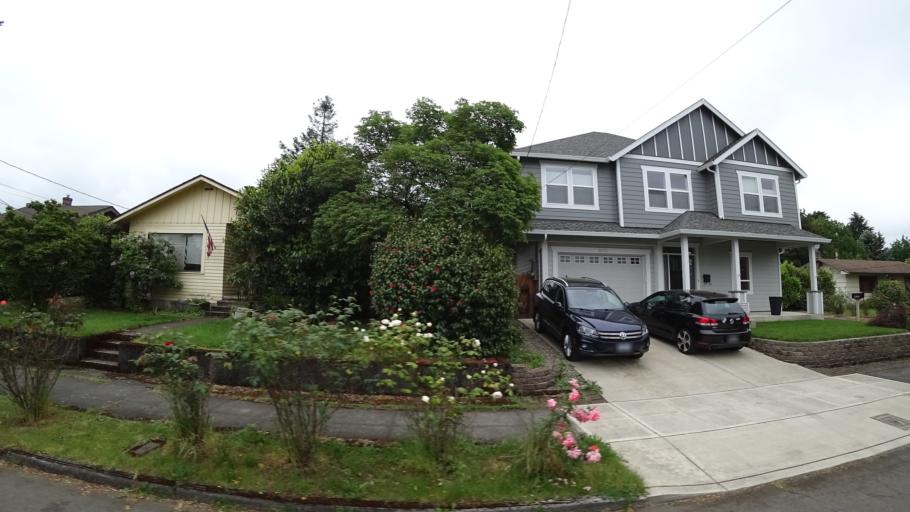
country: US
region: Oregon
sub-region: Multnomah County
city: Portland
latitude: 45.5546
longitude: -122.6131
